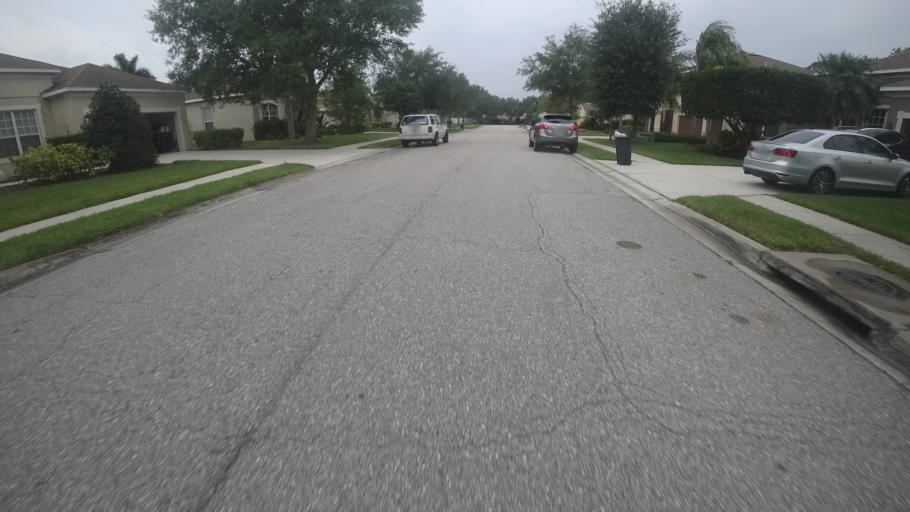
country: US
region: Florida
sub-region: Manatee County
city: Samoset
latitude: 27.4338
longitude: -82.5118
